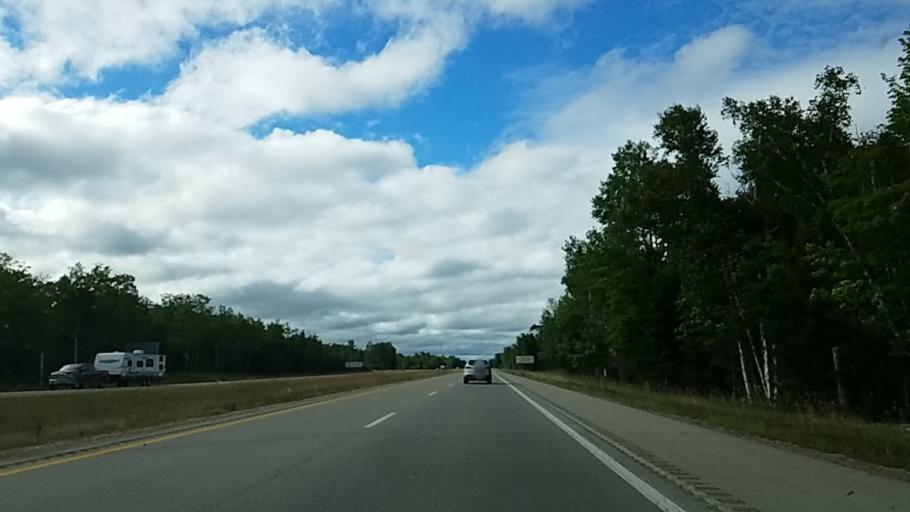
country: US
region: Michigan
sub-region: Mackinac County
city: Saint Ignace
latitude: 45.7472
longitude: -84.7289
